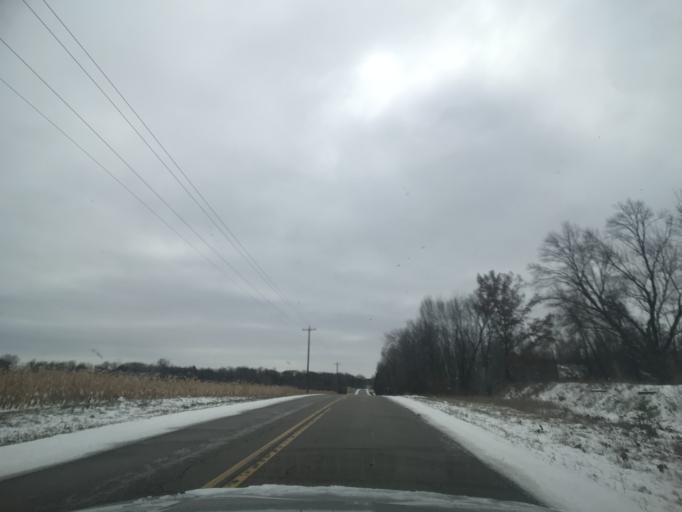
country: US
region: Wisconsin
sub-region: Brown County
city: Suamico
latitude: 44.7166
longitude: -88.0709
